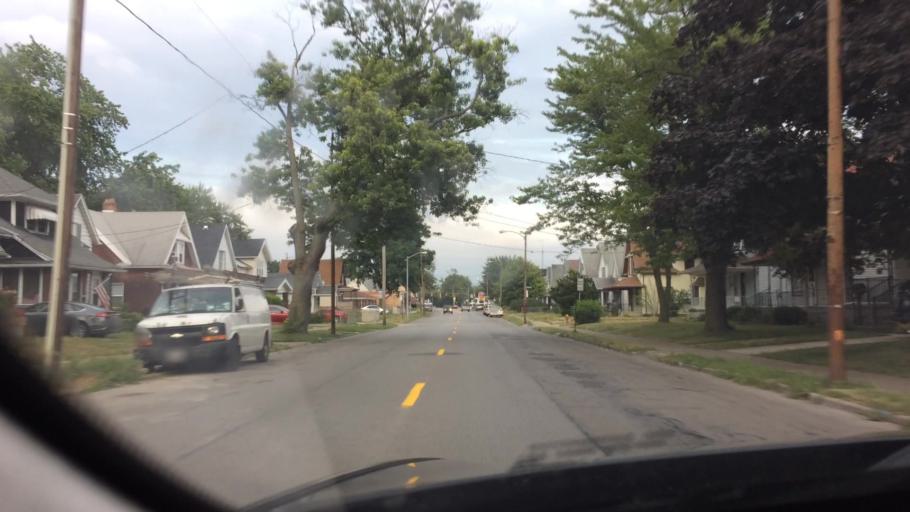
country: US
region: Ohio
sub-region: Wood County
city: Rossford
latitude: 41.6307
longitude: -83.5790
